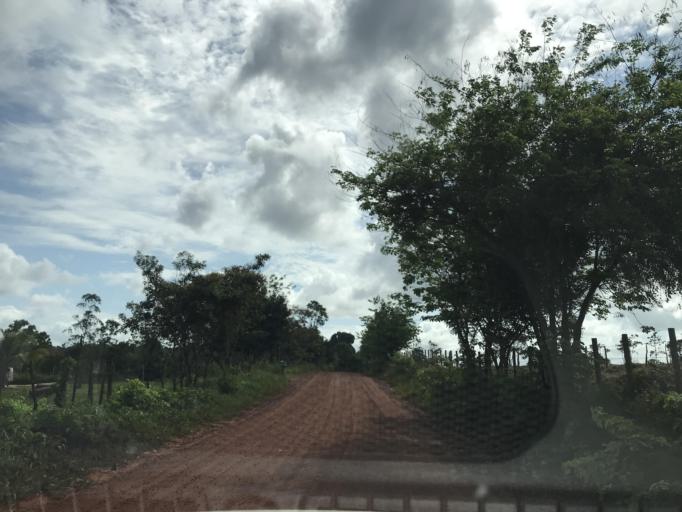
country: BR
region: Bahia
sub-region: Entre Rios
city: Entre Rios
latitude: -12.1734
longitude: -38.1350
